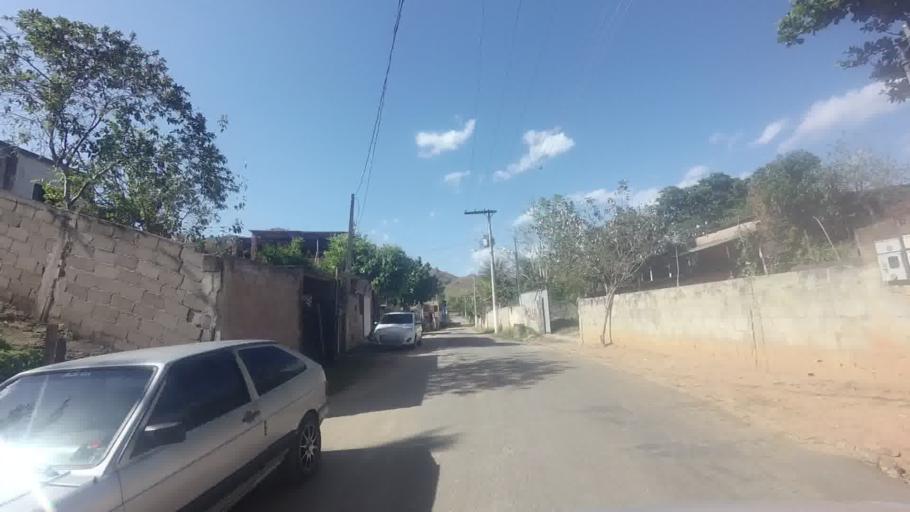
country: BR
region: Rio de Janeiro
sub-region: Bom Jesus Do Itabapoana
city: Bom Jesus do Itabapoana
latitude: -21.1215
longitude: -41.6571
